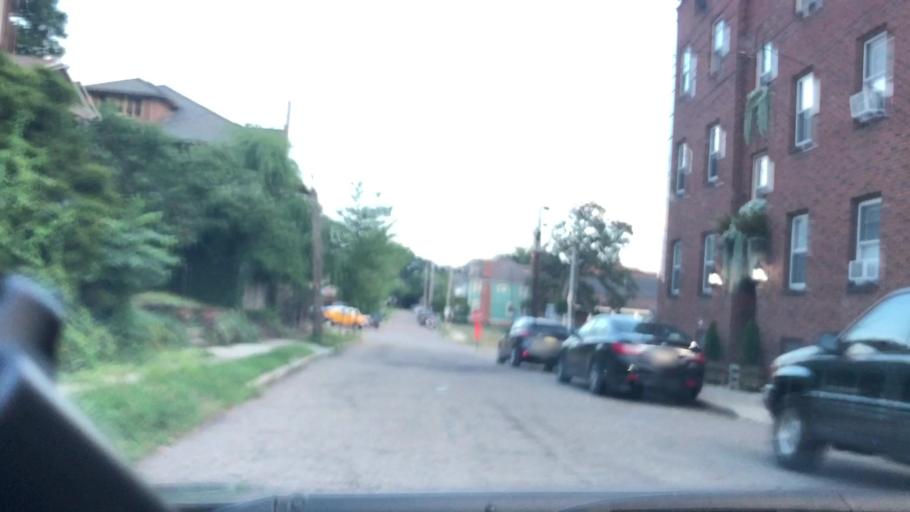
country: US
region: Ohio
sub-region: Stark County
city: Massillon
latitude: 40.7990
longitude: -81.5173
